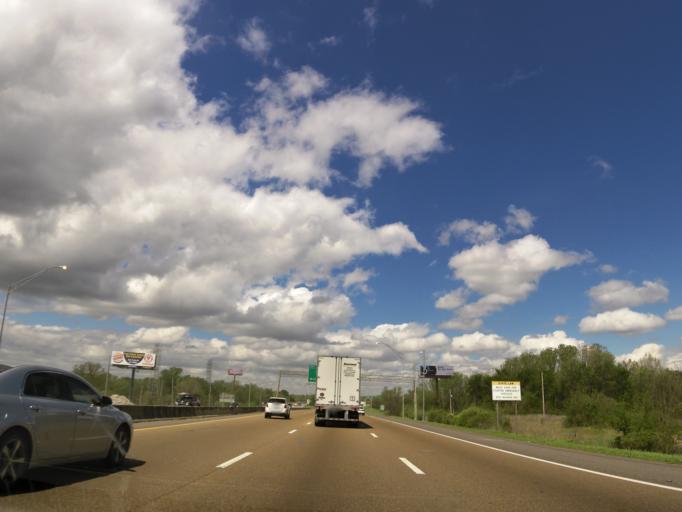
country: US
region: Tennessee
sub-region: Shelby County
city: Memphis
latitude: 35.1817
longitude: -90.0178
